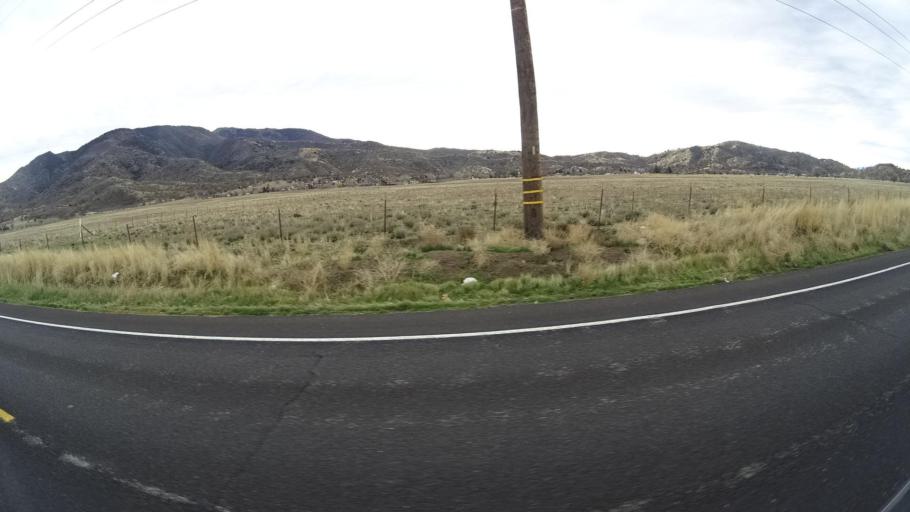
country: US
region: California
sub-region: Kern County
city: Stallion Springs
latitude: 35.0945
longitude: -118.6201
